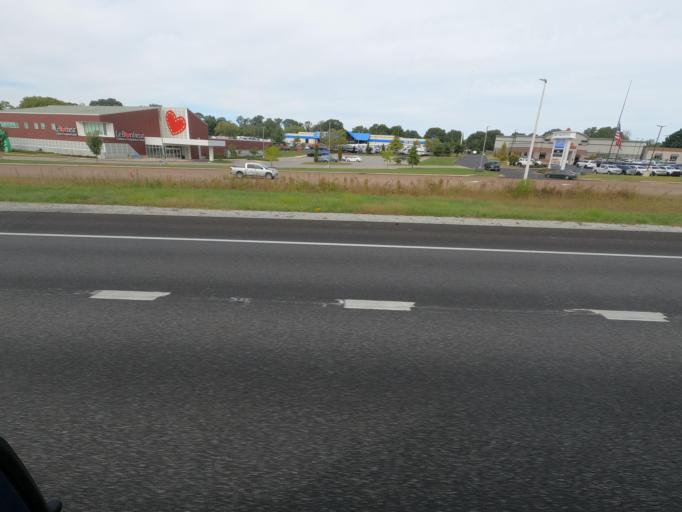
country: US
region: Tennessee
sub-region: Madison County
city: Jackson
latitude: 35.6589
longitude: -88.8693
